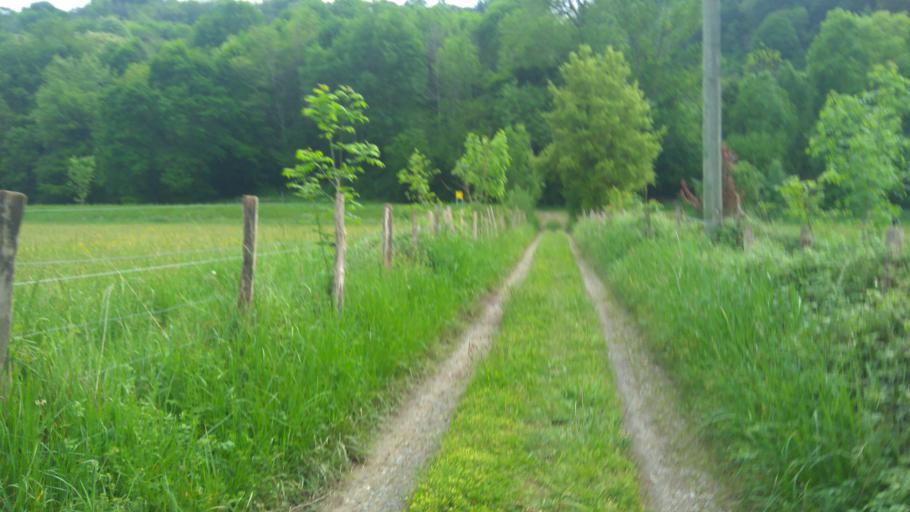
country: FR
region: Aquitaine
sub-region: Departement des Pyrenees-Atlantiques
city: Mazeres-Lezons
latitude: 43.2728
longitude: -0.3529
